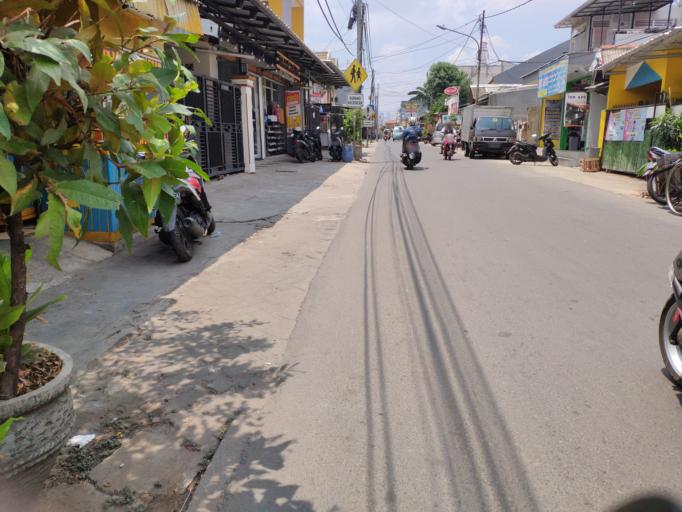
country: ID
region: Jakarta Raya
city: Jakarta
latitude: -6.2112
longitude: 106.8718
